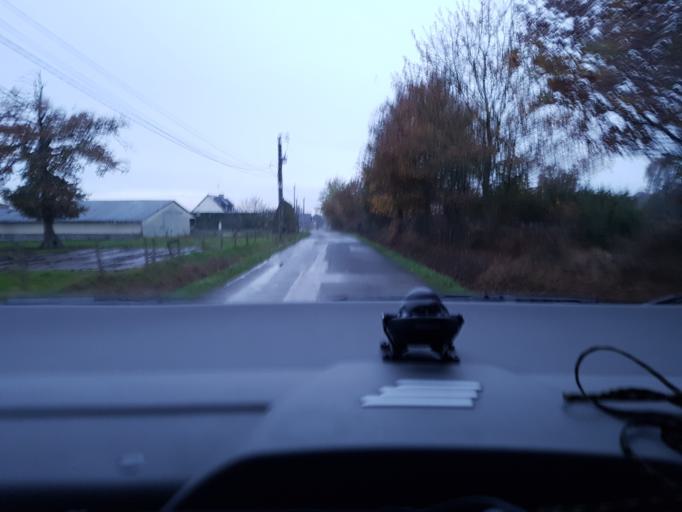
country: FR
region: Brittany
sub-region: Departement d'Ille-et-Vilaine
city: Saint-Aubin-du-Cormier
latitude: 48.2522
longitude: -1.3713
